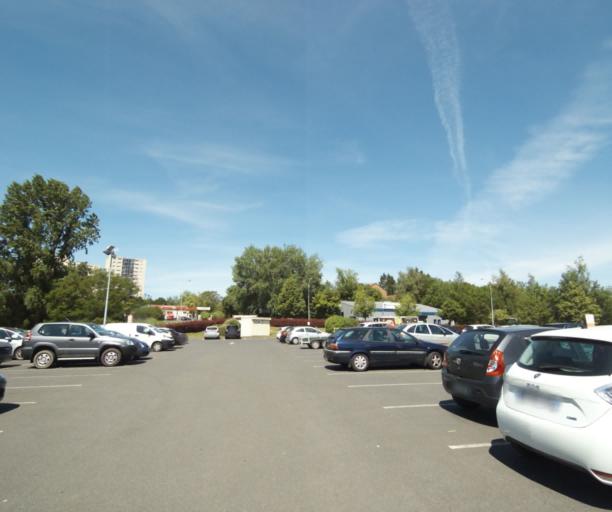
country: FR
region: Champagne-Ardenne
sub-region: Departement des Ardennes
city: Villers-Semeuse
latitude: 49.7458
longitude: 4.7285
